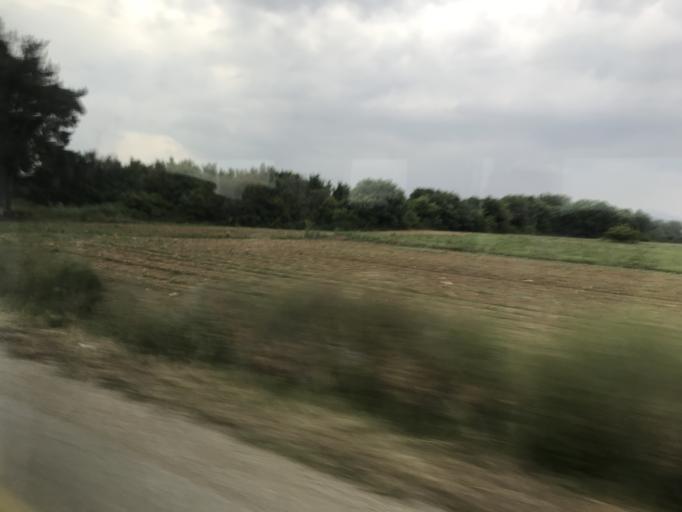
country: GR
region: East Macedonia and Thrace
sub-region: Nomos Rodopis
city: Aratos
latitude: 41.0867
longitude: 25.5195
